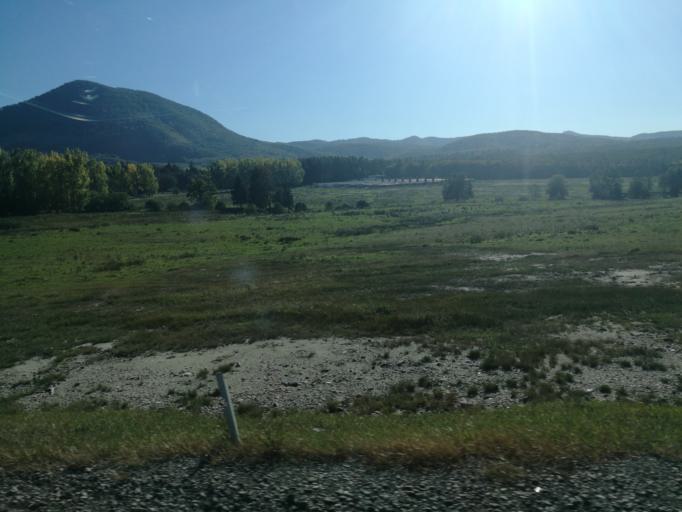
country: RO
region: Brasov
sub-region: Comuna Dumbravita
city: Dumbravita
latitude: 45.7481
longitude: 25.4117
